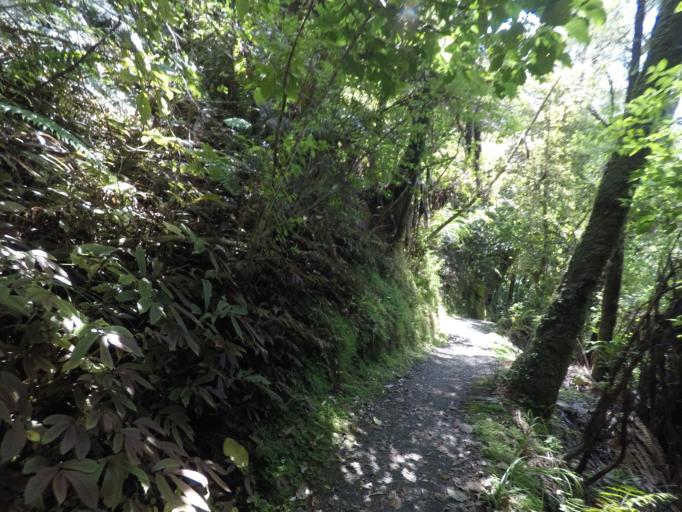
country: NZ
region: Auckland
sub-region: Auckland
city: Warkworth
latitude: -36.4534
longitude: 174.6513
